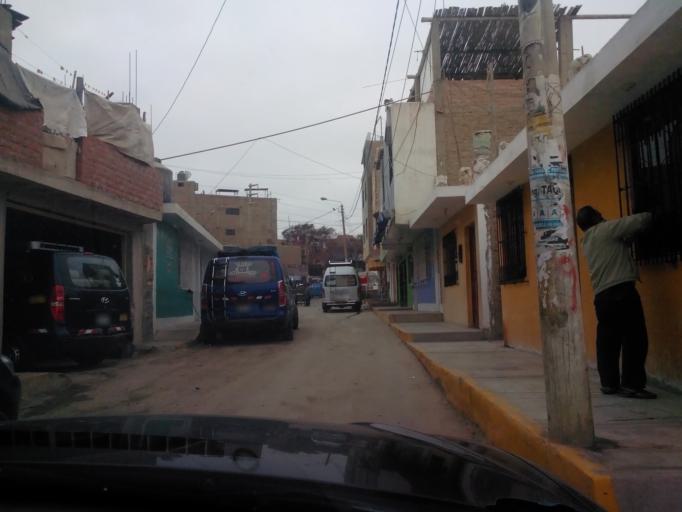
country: PE
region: Ica
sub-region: Provincia de Pisco
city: San Clemente
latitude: -13.6837
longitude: -76.1593
